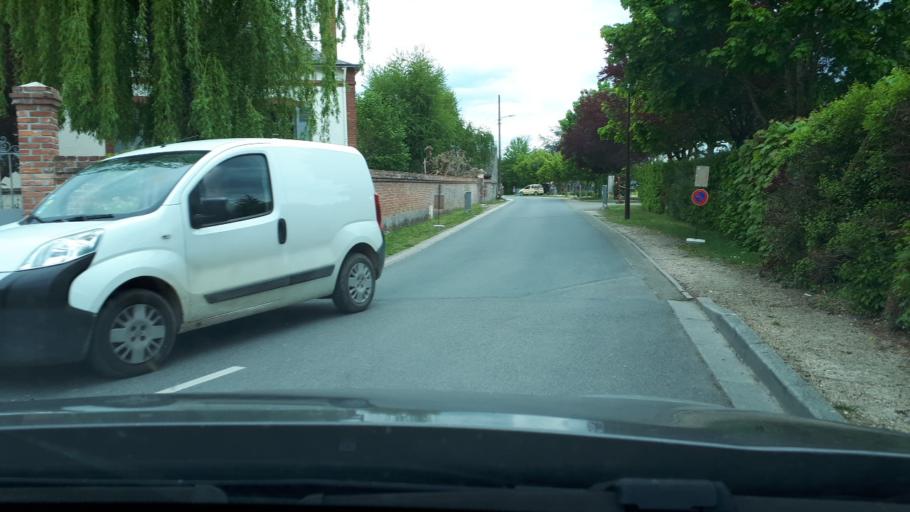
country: FR
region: Centre
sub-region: Departement du Loir-et-Cher
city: Souesmes
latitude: 47.5143
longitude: 2.1493
